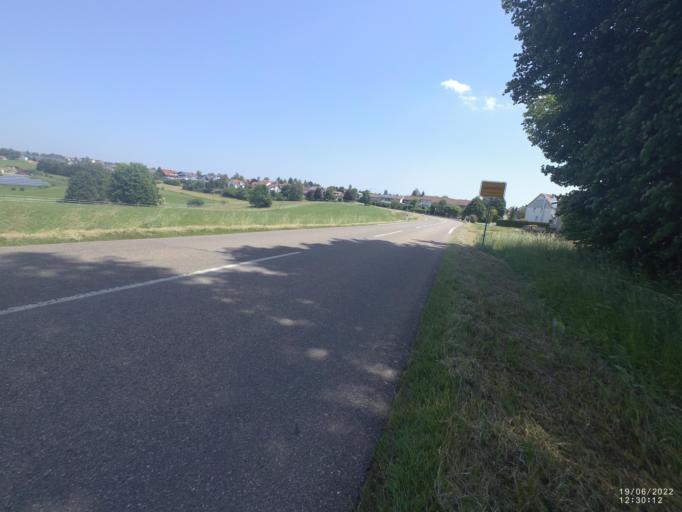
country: DE
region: Baden-Wuerttemberg
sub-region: Regierungsbezirk Stuttgart
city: Gerstetten
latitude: 48.6165
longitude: 10.0084
